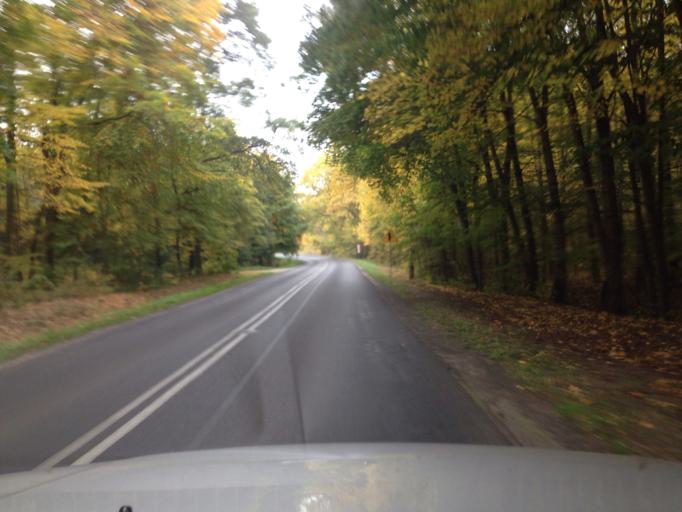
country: PL
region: Kujawsko-Pomorskie
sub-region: Powiat brodnicki
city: Brodnica
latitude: 53.2642
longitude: 19.3322
